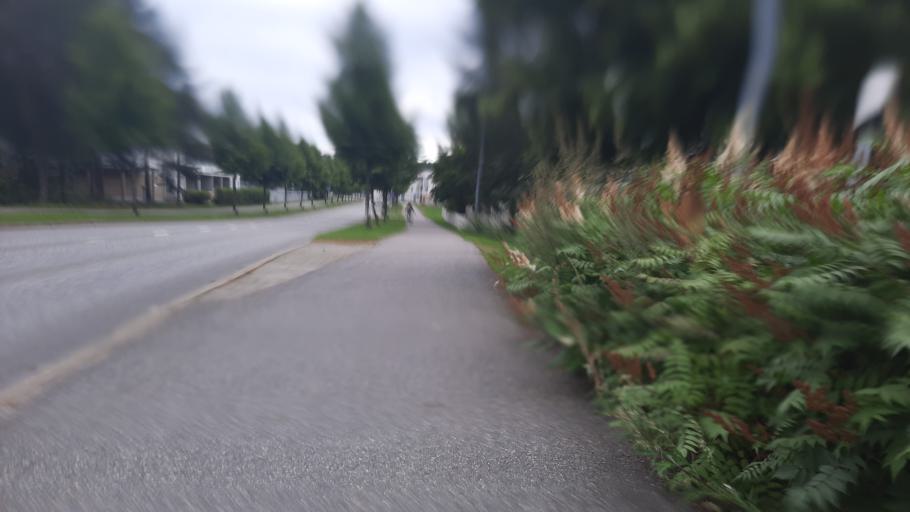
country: FI
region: North Karelia
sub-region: Joensuu
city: Joensuu
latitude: 62.6255
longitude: 29.8546
